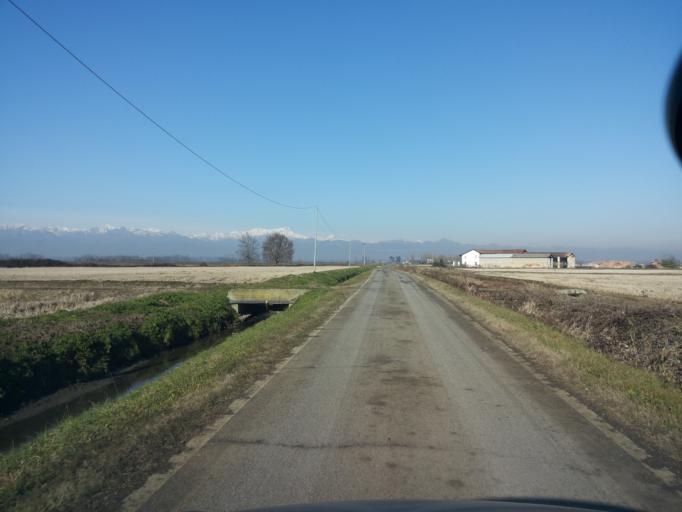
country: IT
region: Piedmont
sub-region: Provincia di Vercelli
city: San Germano Vercellese
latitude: 45.3620
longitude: 8.2434
